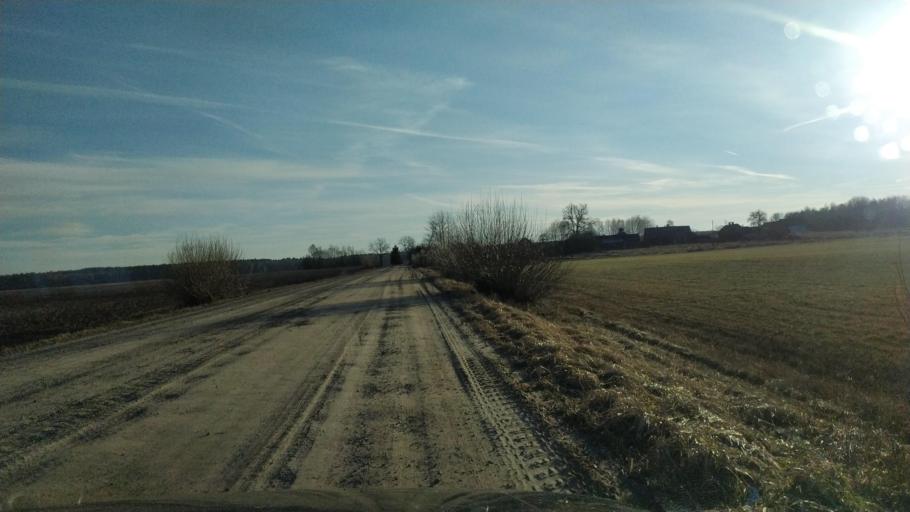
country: BY
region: Brest
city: Pruzhany
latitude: 52.5530
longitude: 24.2953
